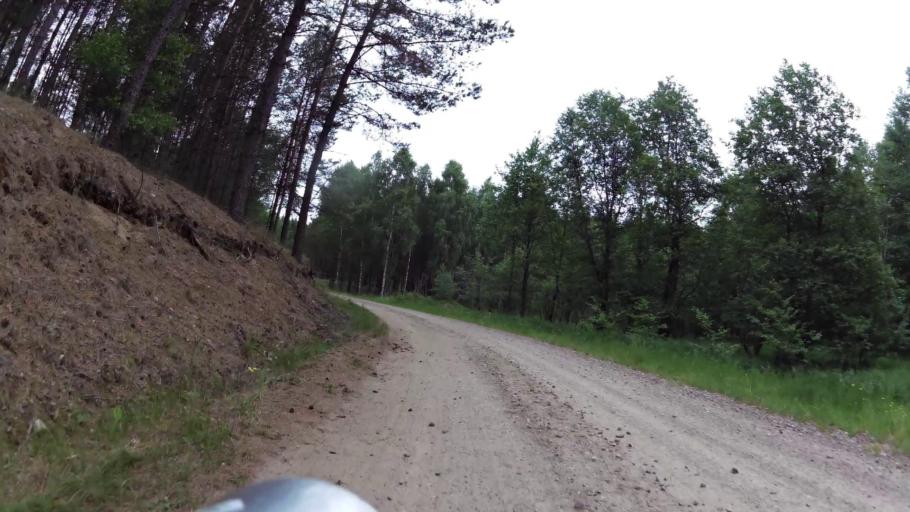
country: PL
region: West Pomeranian Voivodeship
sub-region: Powiat szczecinecki
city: Bialy Bor
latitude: 53.9514
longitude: 16.8338
